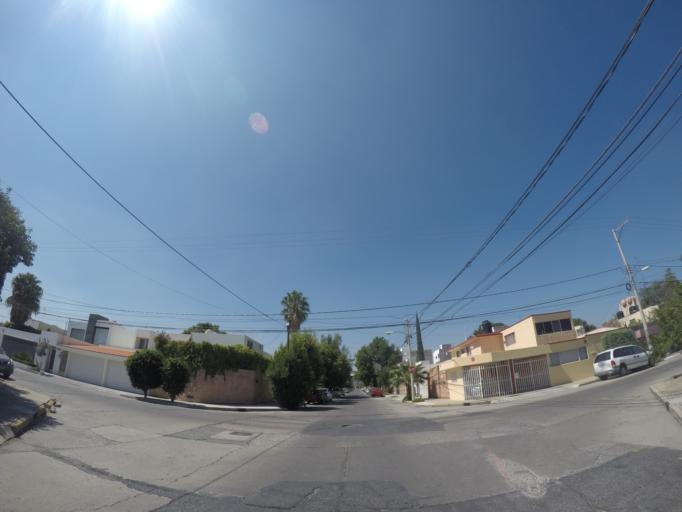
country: MX
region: San Luis Potosi
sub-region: San Luis Potosi
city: San Luis Potosi
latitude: 22.1440
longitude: -101.0070
